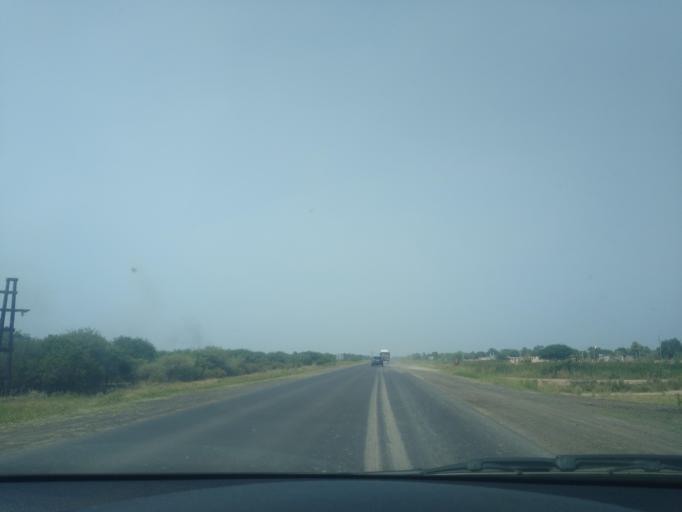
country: AR
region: Chaco
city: Fontana
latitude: -27.4902
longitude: -59.0727
